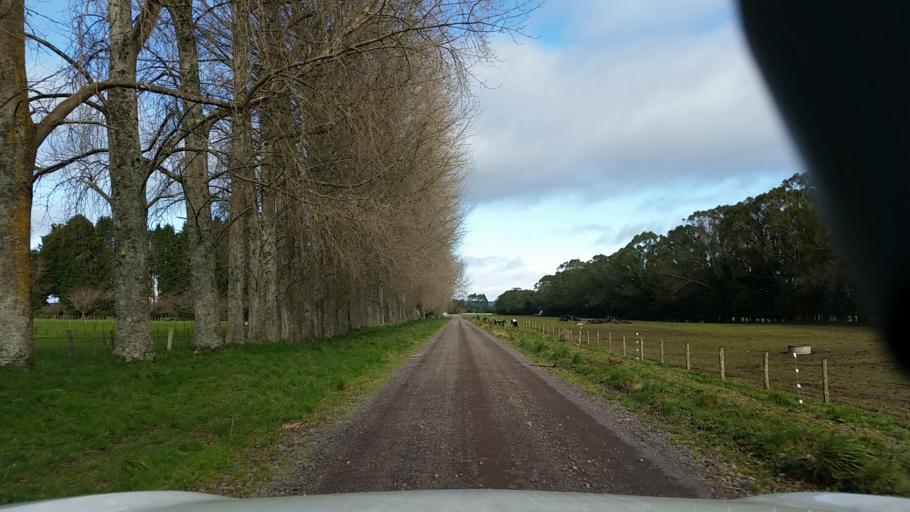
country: NZ
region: Bay of Plenty
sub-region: Whakatane District
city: Murupara
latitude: -38.4690
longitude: 176.4174
